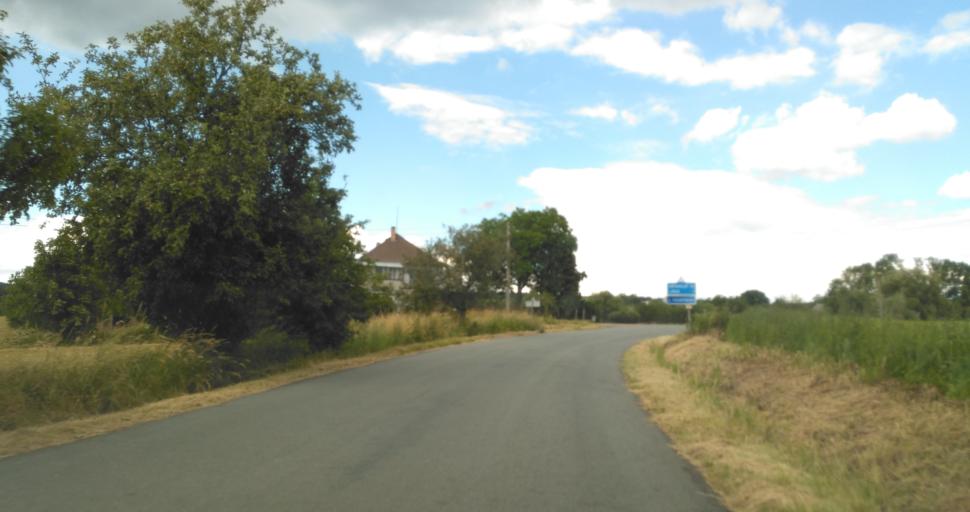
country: CZ
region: Plzensky
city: Zbiroh
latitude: 49.8816
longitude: 13.8004
